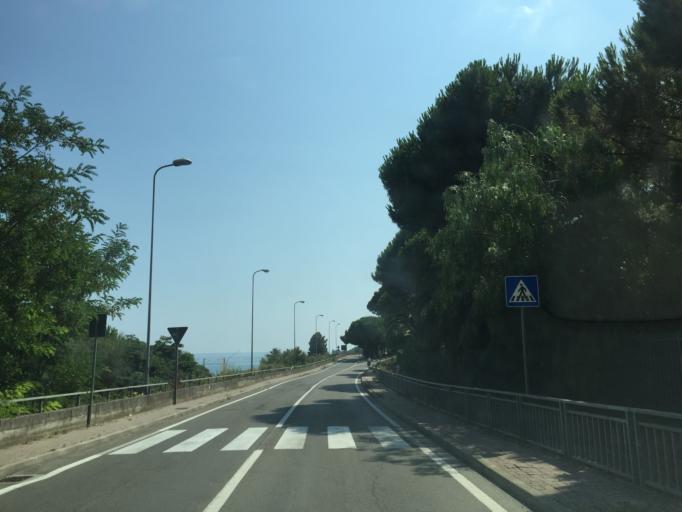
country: IT
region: Liguria
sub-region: Provincia di Imperia
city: Ventimiglia
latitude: 43.7924
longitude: 7.5628
